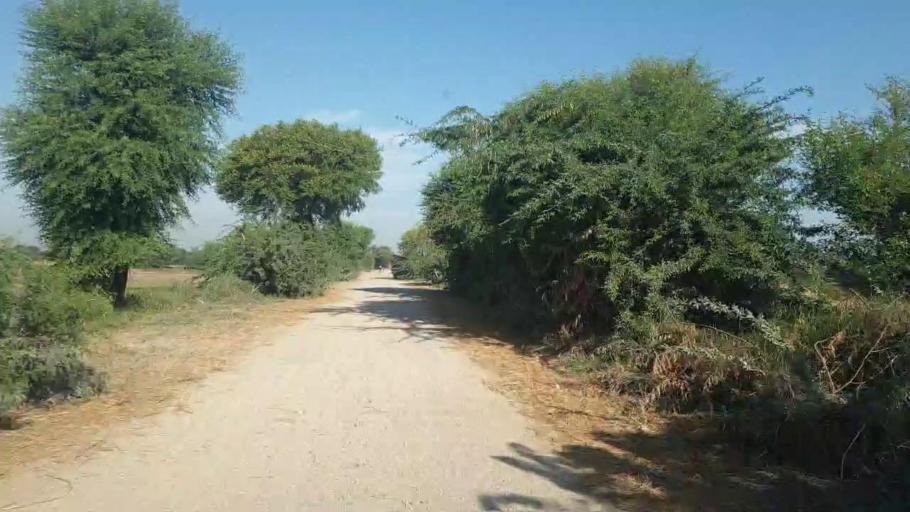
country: PK
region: Sindh
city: Talhar
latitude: 24.9425
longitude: 68.7882
